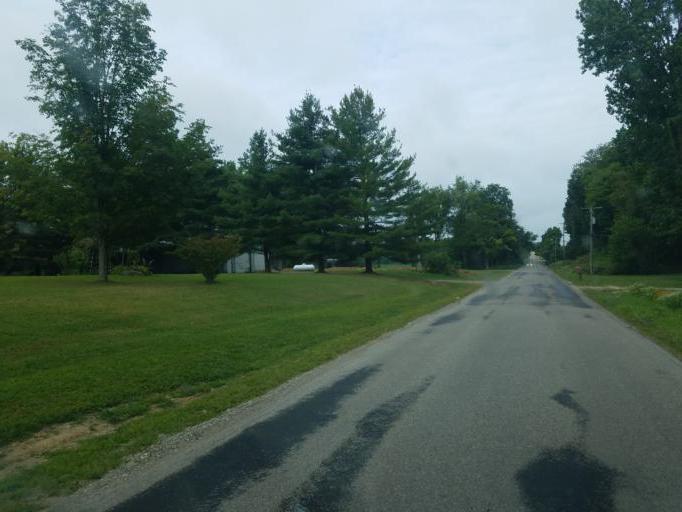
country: US
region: Ohio
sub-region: Morrow County
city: Cardington
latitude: 40.4116
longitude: -82.8152
